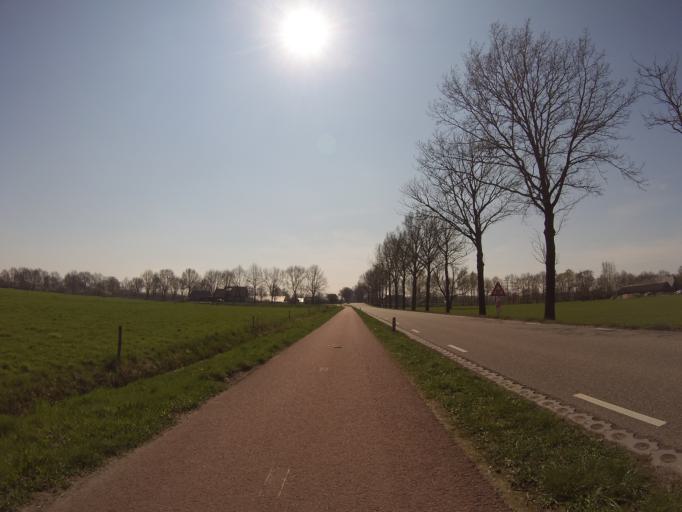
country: NL
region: Utrecht
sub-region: Gemeente Utrechtse Heuvelrug
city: Overberg
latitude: 52.0528
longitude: 5.4919
